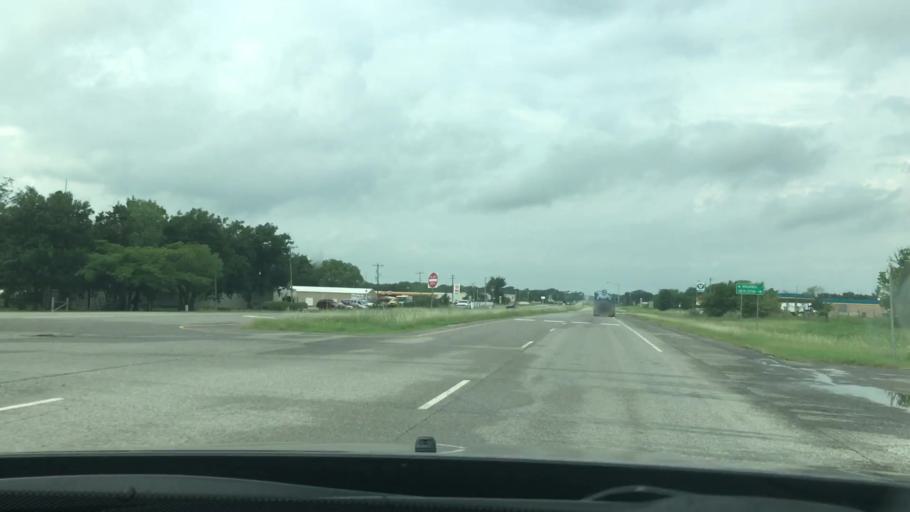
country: US
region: Oklahoma
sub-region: Carter County
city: Wilson
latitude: 34.1731
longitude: -97.4717
